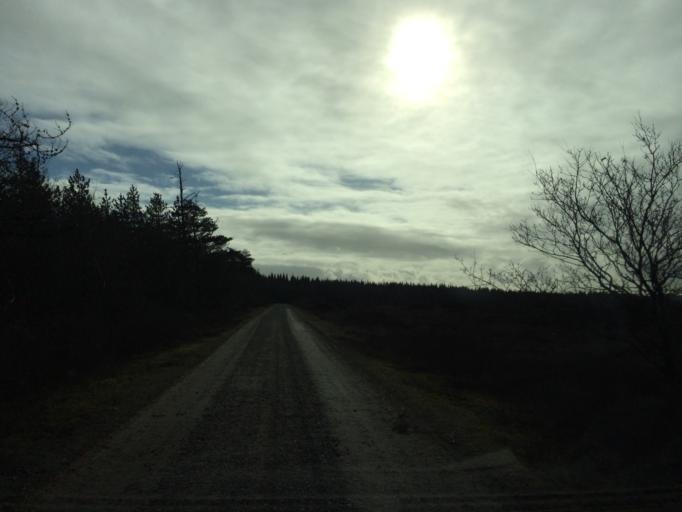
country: DK
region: Central Jutland
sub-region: Holstebro Kommune
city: Ulfborg
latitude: 56.2593
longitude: 8.4250
